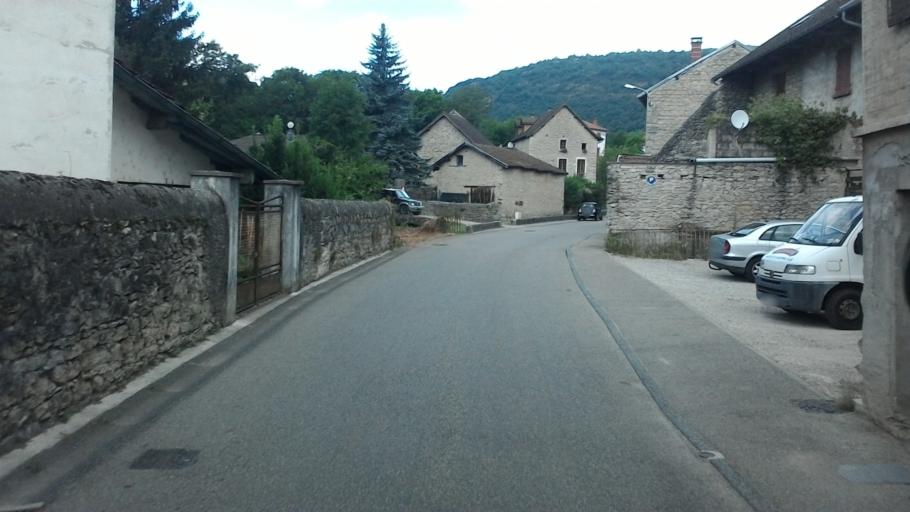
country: FR
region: Rhone-Alpes
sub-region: Departement de l'Ain
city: Villebois
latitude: 45.8500
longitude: 5.4342
